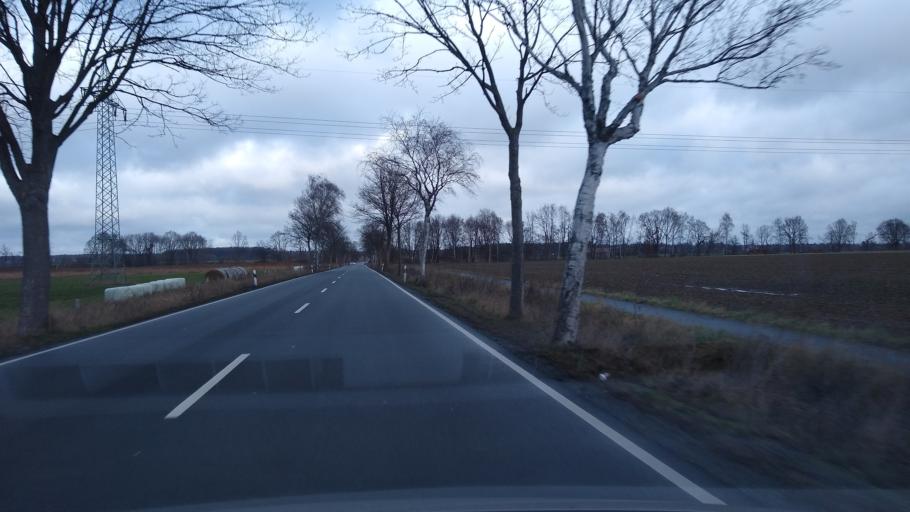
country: DE
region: Lower Saxony
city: Edemissen
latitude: 52.3682
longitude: 10.2491
